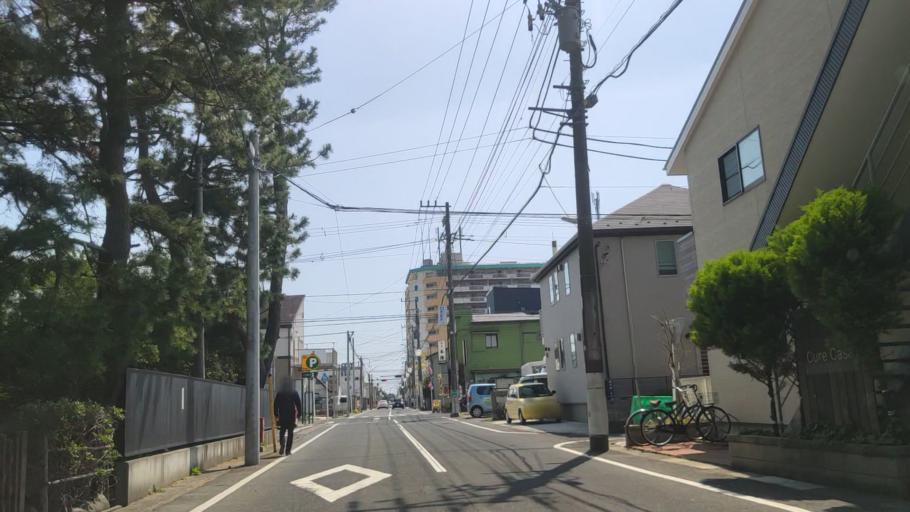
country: JP
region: Kanagawa
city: Hiratsuka
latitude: 35.3199
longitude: 139.3390
